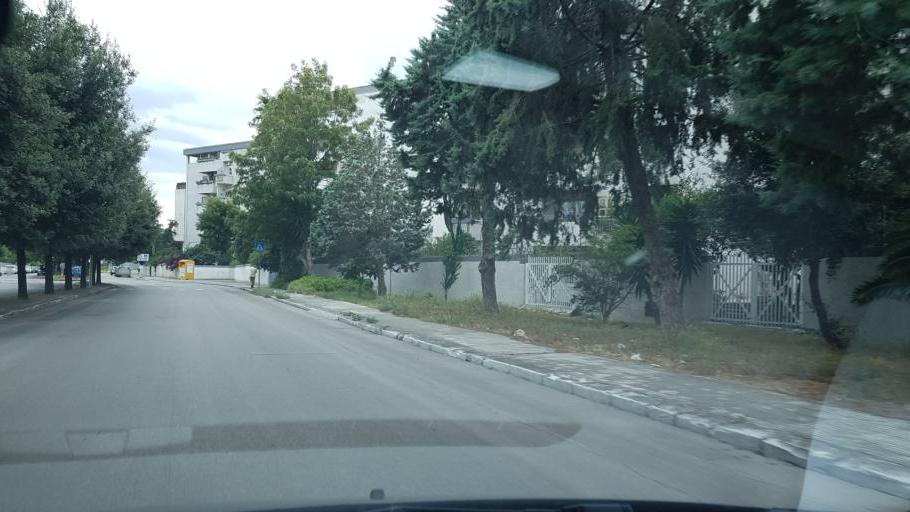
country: IT
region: Apulia
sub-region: Provincia di Brindisi
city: Brindisi
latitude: 40.6245
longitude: 17.9425
